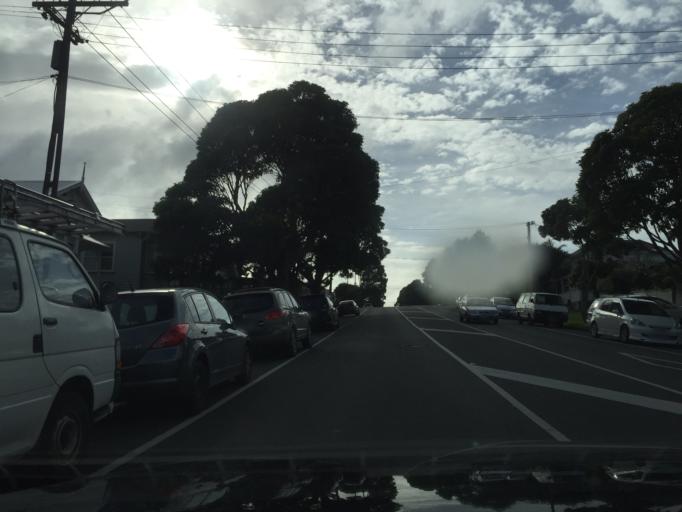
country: NZ
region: Auckland
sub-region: Auckland
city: Auckland
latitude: -36.8612
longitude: 174.7437
